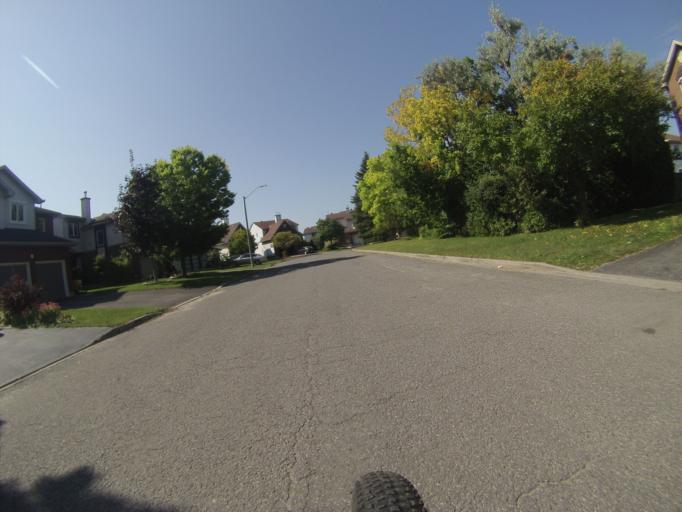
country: CA
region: Ontario
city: Ottawa
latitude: 45.3649
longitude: -75.6218
